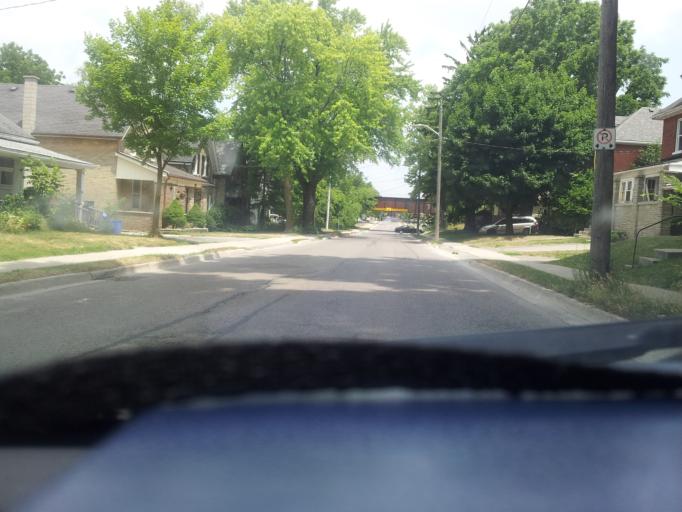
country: CA
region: Ontario
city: Stratford
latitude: 43.3662
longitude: -80.9859
